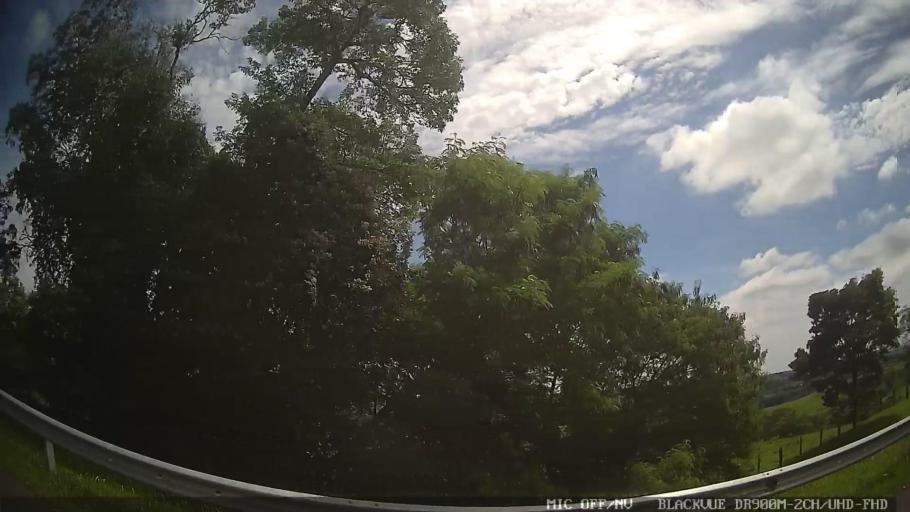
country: BR
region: Sao Paulo
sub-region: Laranjal Paulista
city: Laranjal Paulista
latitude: -23.0845
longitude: -47.7860
